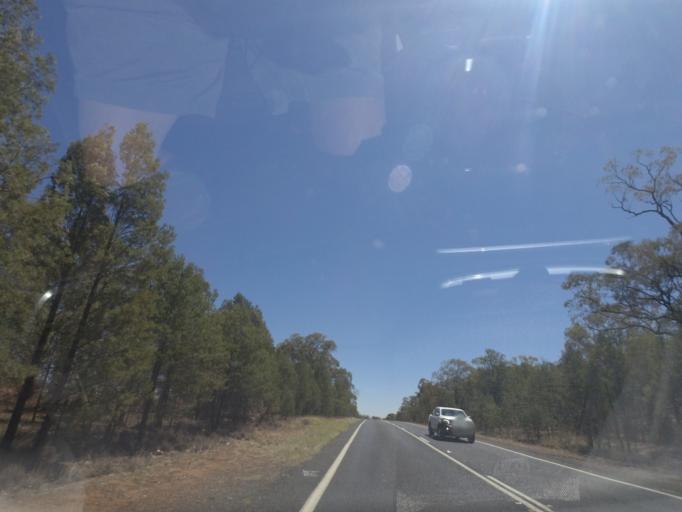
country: AU
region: New South Wales
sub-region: Gilgandra
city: Gilgandra
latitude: -31.4746
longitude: 148.8982
